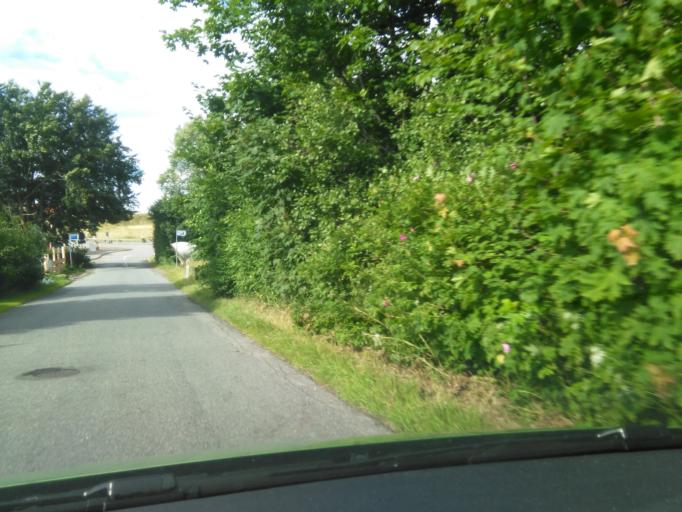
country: DK
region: Central Jutland
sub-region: Horsens Kommune
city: Braedstrup
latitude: 55.9804
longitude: 9.7239
